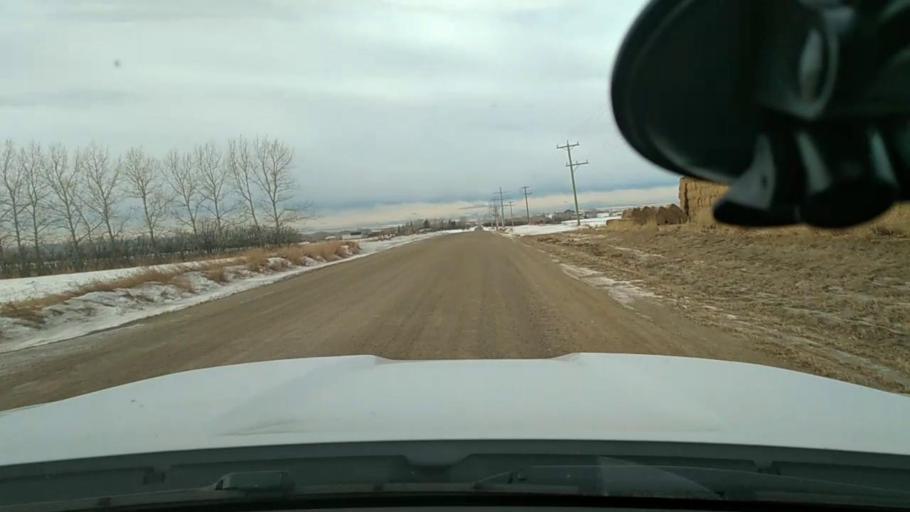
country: CA
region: Alberta
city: Airdrie
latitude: 51.2417
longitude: -113.9530
